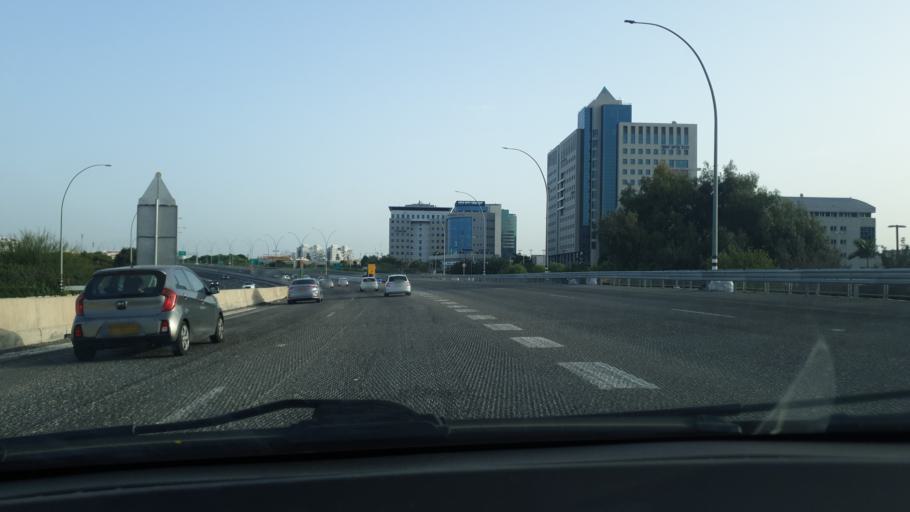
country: IL
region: Central District
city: Ra'anana
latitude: 32.1990
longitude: 34.8847
